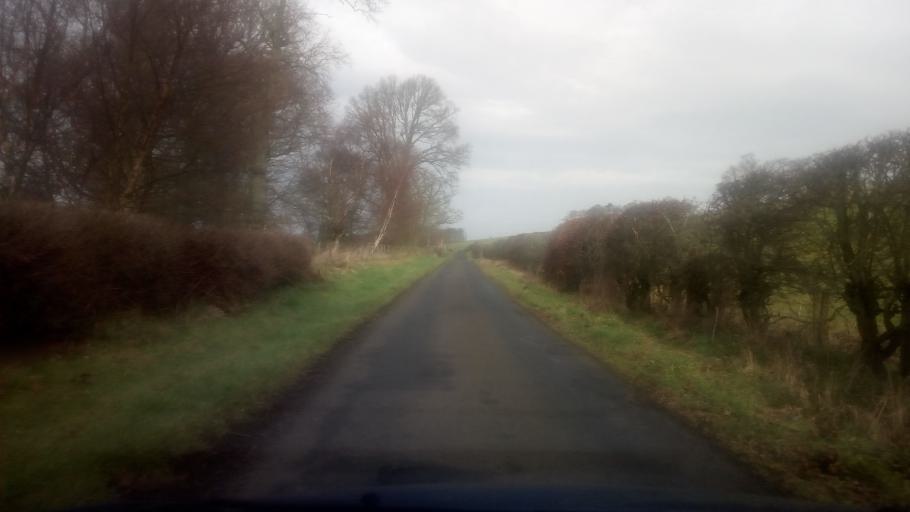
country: GB
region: Scotland
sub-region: The Scottish Borders
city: Jedburgh
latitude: 55.4402
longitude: -2.6302
